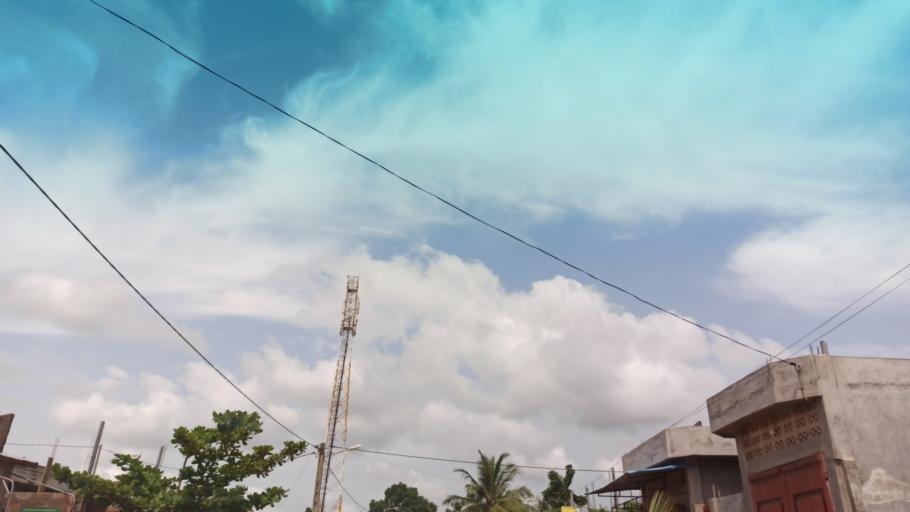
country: BJ
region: Queme
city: Porto-Novo
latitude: 6.4996
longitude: 2.5870
